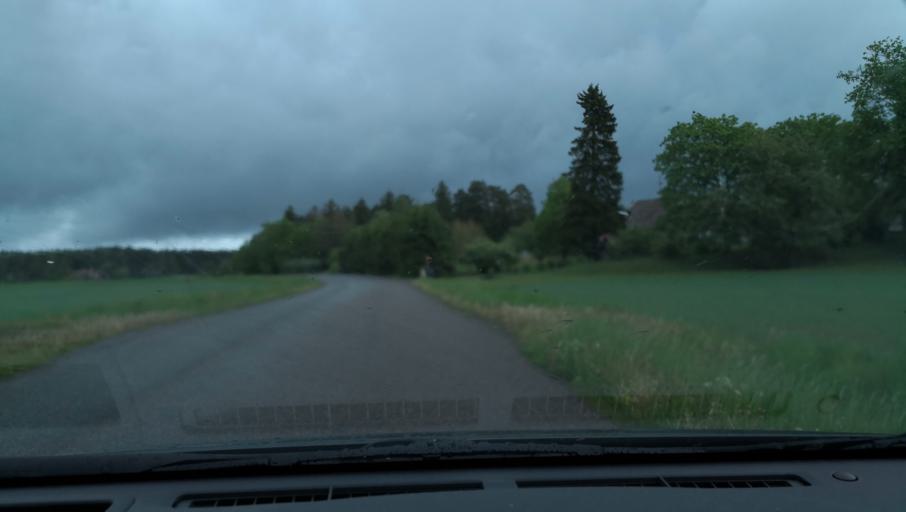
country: SE
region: Uppsala
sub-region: Enkopings Kommun
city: Orsundsbro
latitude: 59.8136
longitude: 17.3870
